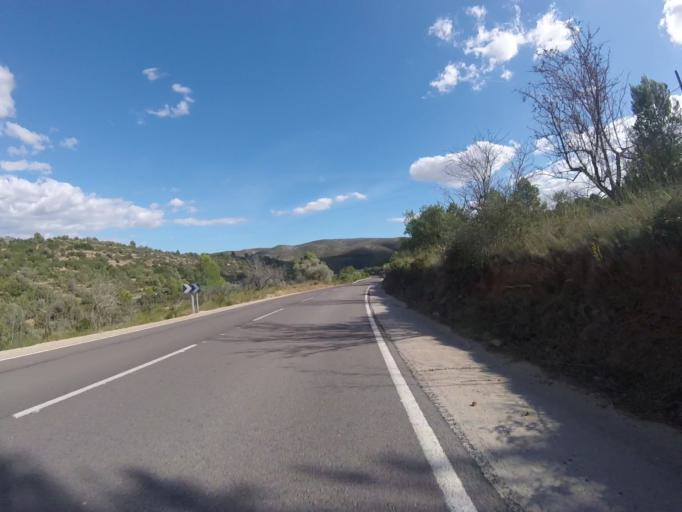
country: ES
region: Valencia
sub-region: Provincia de Castello
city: Cuevas de Vinroma
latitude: 40.3055
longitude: 0.1597
